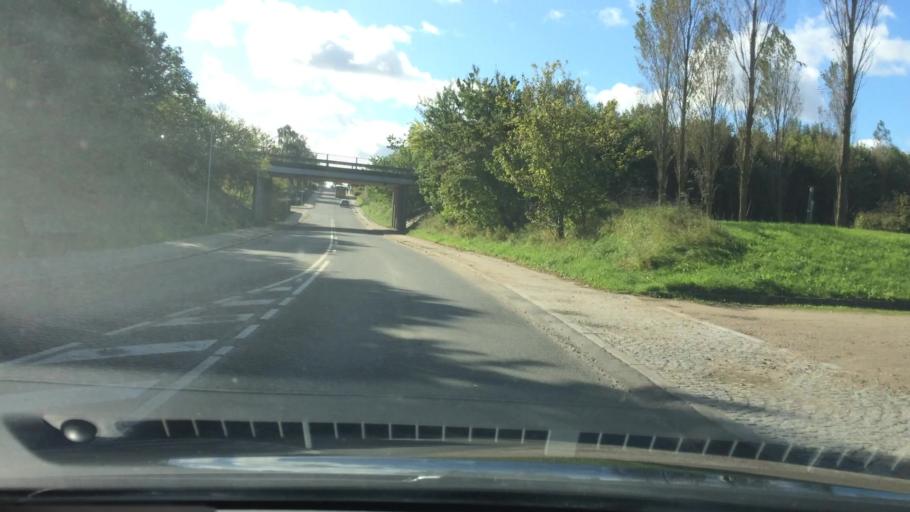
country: DK
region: Central Jutland
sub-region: Horsens Kommune
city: Horsens
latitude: 55.8760
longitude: 9.9146
